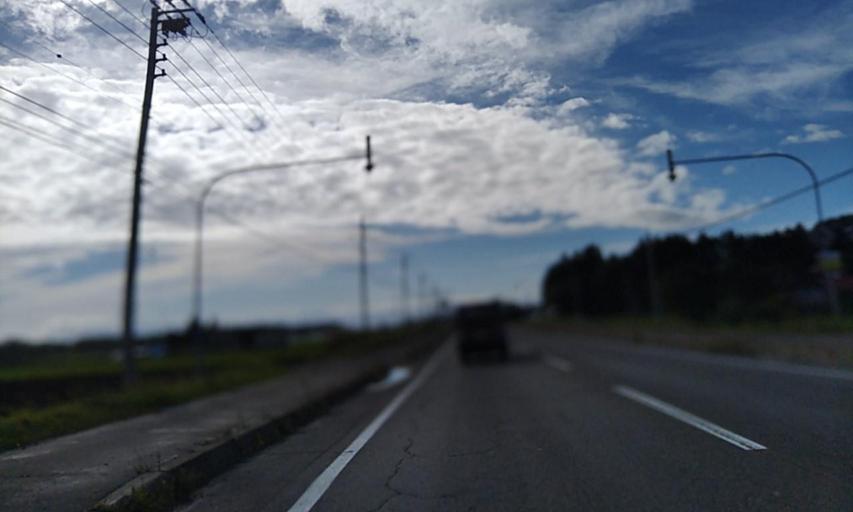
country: JP
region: Hokkaido
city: Obihiro
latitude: 42.9212
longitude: 143.3306
